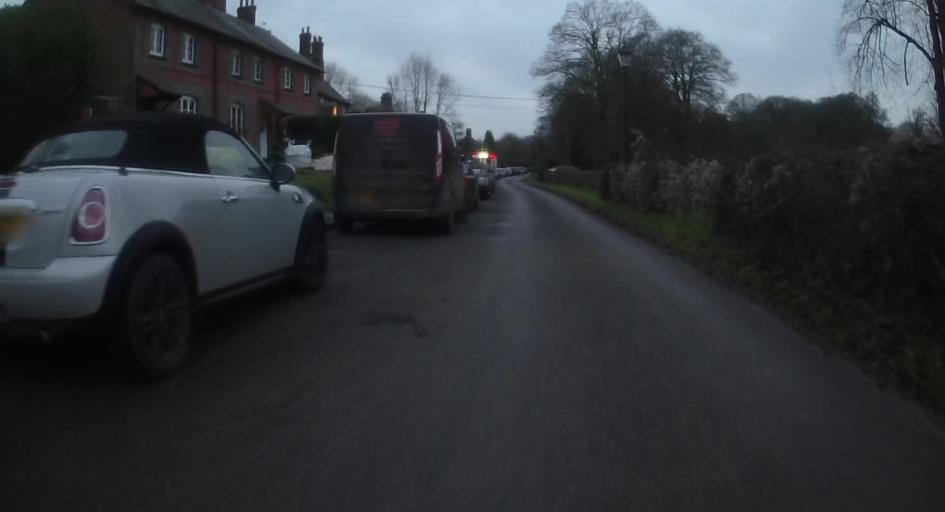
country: GB
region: England
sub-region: Hampshire
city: Overton
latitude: 51.2333
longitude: -1.2981
